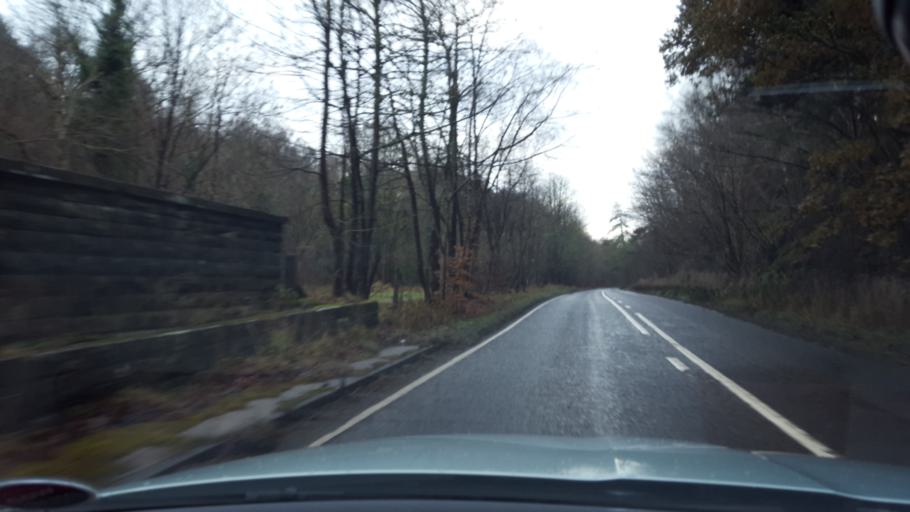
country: GB
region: Scotland
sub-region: Perth and Kinross
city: Bridge of Earn
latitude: 56.2997
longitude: -3.3731
